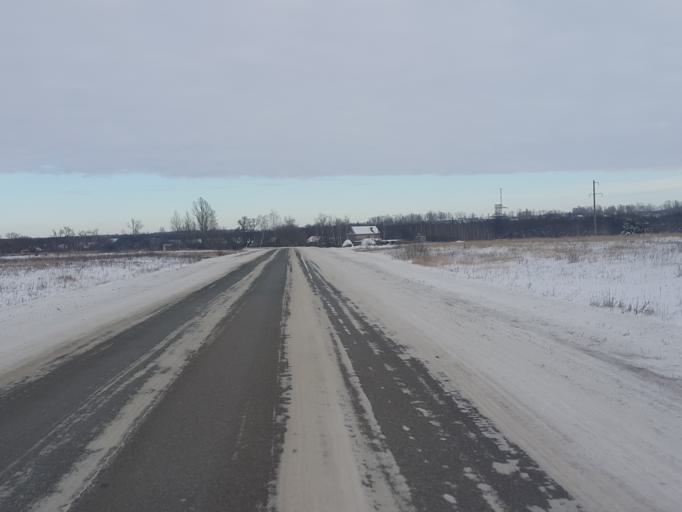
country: RU
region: Tambov
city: Platonovka
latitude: 52.8703
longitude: 41.8654
